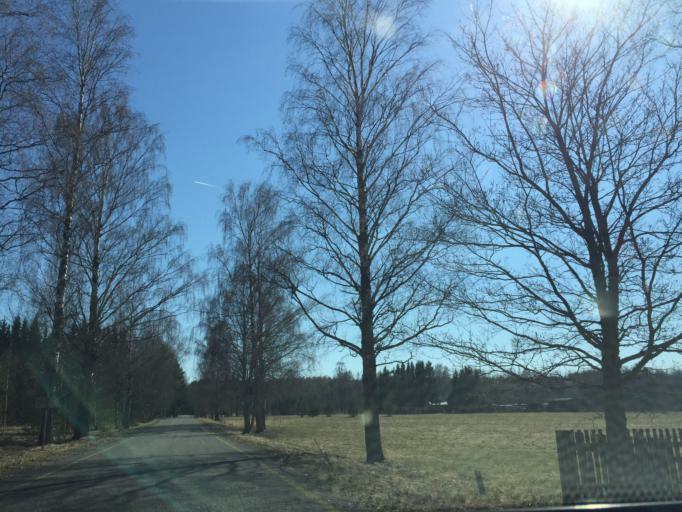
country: EE
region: Jogevamaa
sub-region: Mustvee linn
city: Mustvee
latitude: 58.9964
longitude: 27.2264
